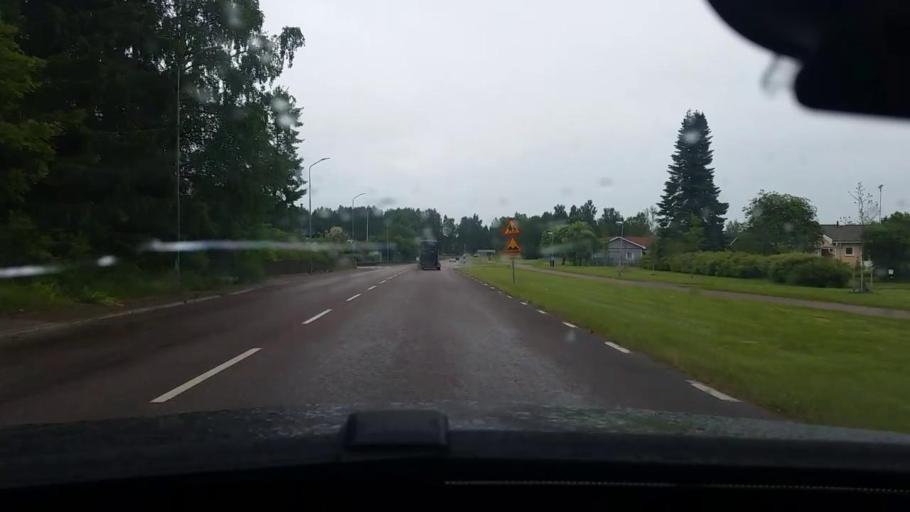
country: SE
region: Dalarna
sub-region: Borlange Kommun
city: Borlaenge
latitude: 60.4892
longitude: 15.3925
